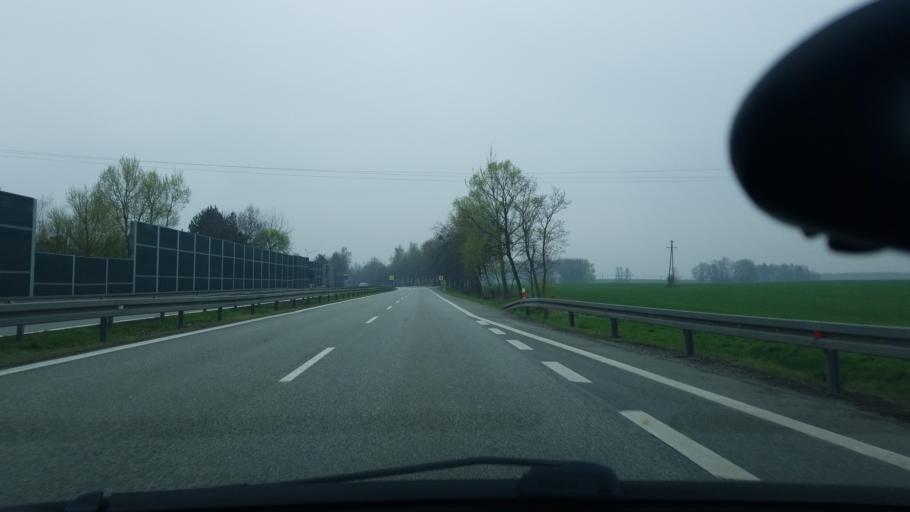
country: PL
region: Silesian Voivodeship
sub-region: Powiat pszczynski
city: Pawlowice
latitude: 49.9847
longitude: 18.7136
